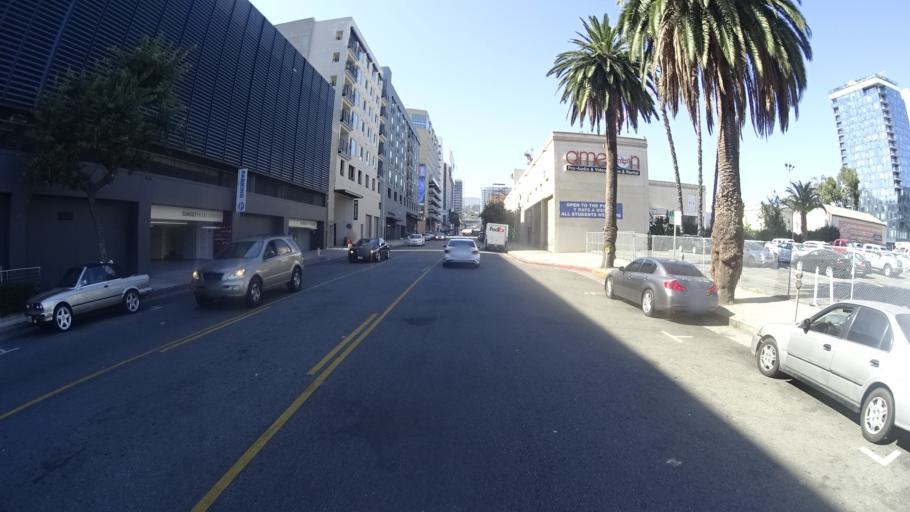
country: US
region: California
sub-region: Los Angeles County
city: Hollywood
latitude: 34.0987
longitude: -118.3251
